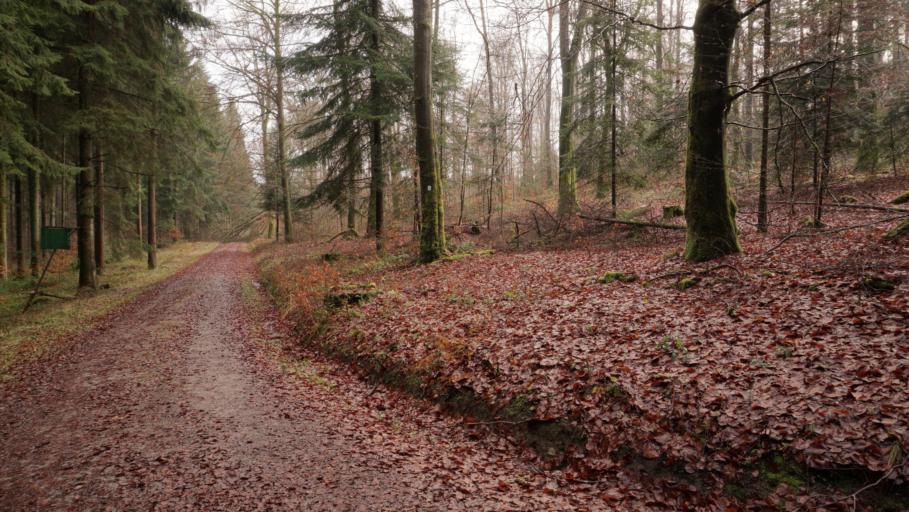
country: DE
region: Baden-Wuerttemberg
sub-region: Karlsruhe Region
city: Reichartshausen
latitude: 49.4019
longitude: 8.9550
